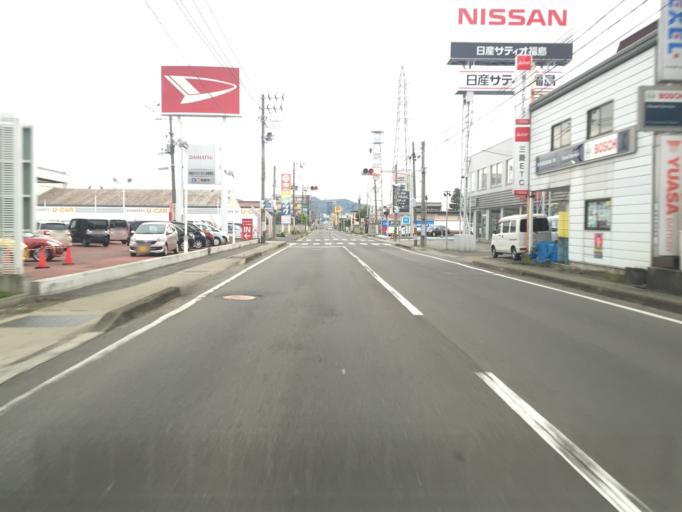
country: JP
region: Fukushima
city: Fukushima-shi
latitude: 37.7343
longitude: 140.4604
